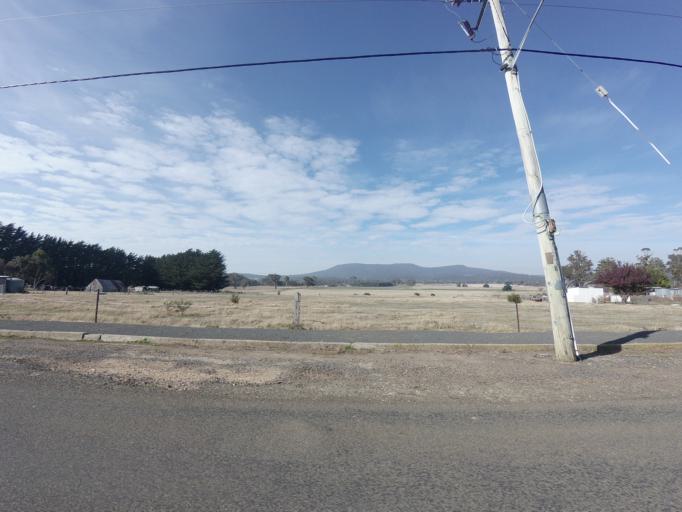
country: AU
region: Tasmania
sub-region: Sorell
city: Sorell
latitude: -42.4547
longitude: 147.4616
